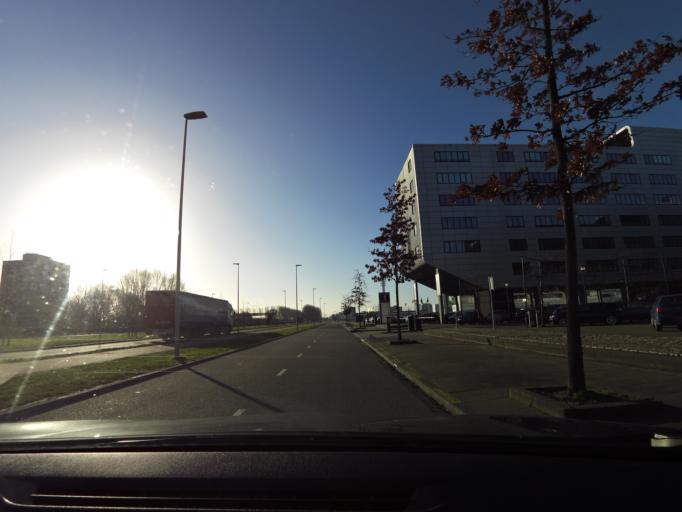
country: NL
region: South Holland
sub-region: Gemeente Rotterdam
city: Delfshaven
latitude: 51.8868
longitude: 4.4577
